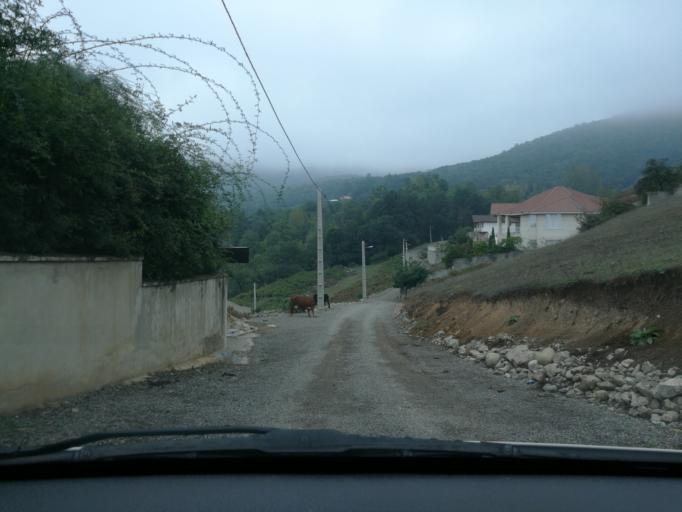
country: IR
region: Mazandaran
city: `Abbasabad
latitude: 36.4978
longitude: 51.2065
